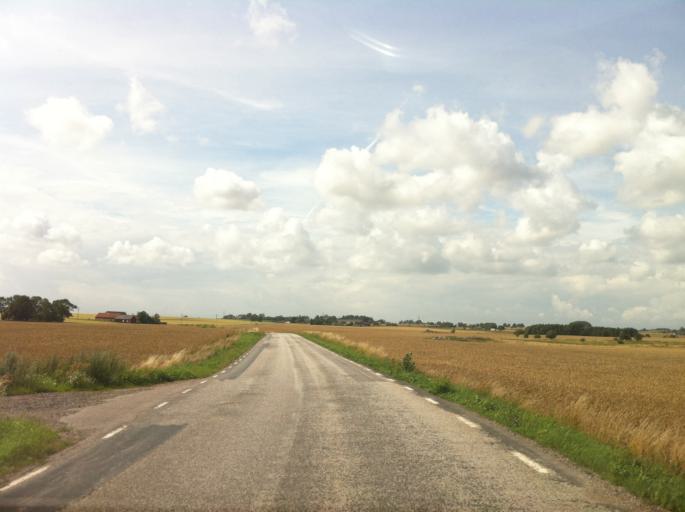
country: SE
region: Skane
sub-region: Trelleborgs Kommun
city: Anderslov
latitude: 55.5036
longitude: 13.3994
